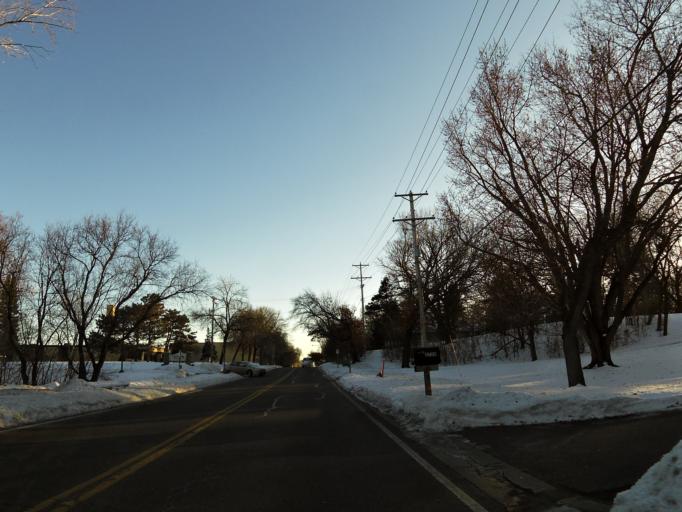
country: US
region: Minnesota
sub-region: Ramsey County
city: North Saint Paul
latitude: 45.0248
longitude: -93.0356
